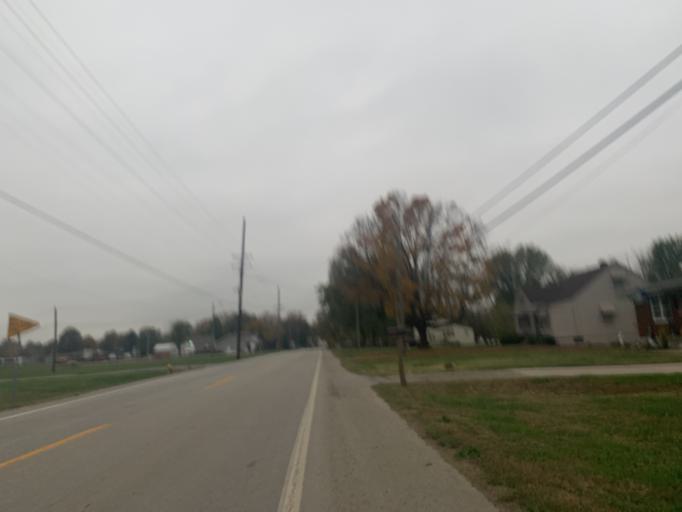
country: US
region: Kentucky
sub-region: Jefferson County
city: Shively
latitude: 38.2141
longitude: -85.8266
